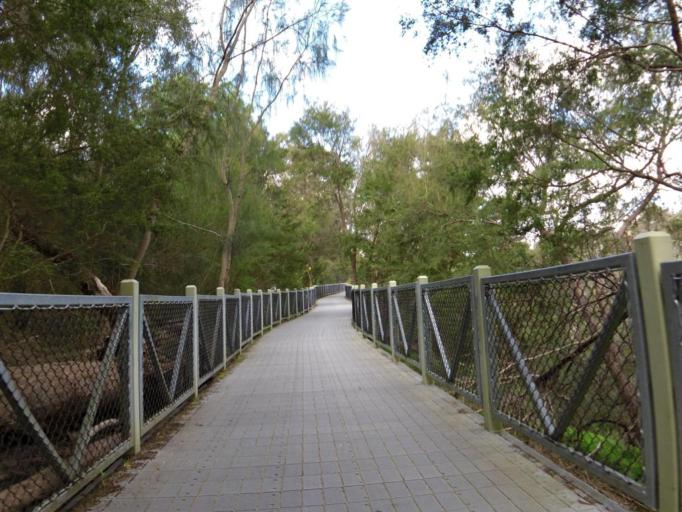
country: AU
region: Victoria
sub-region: Banyule
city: Darch
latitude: -37.7522
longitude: 145.1180
